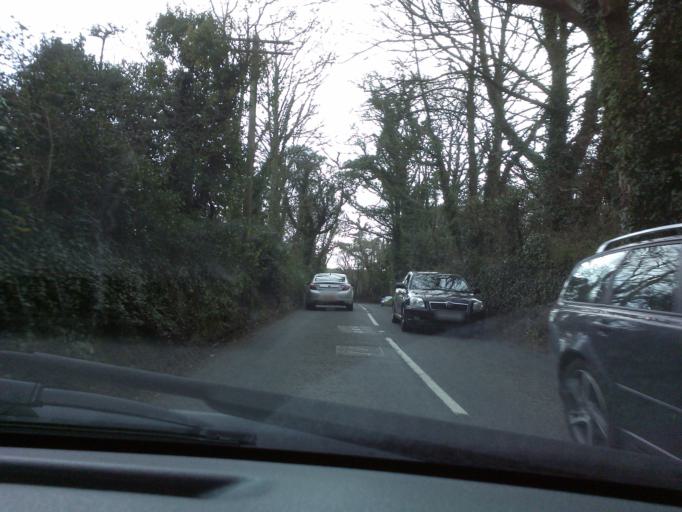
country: GB
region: England
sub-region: Cornwall
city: Penzance
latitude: 50.1084
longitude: -5.5680
